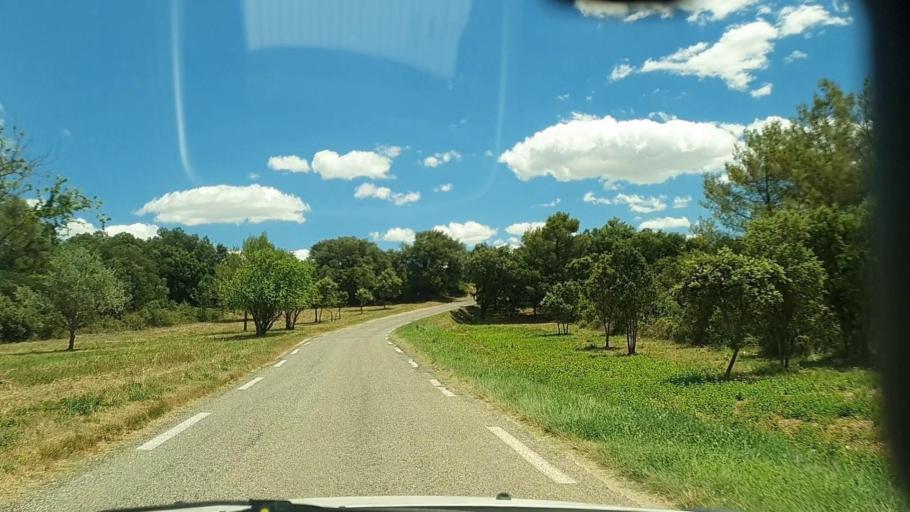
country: FR
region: Languedoc-Roussillon
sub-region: Departement du Gard
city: Cabrieres
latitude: 43.9103
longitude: 4.4476
